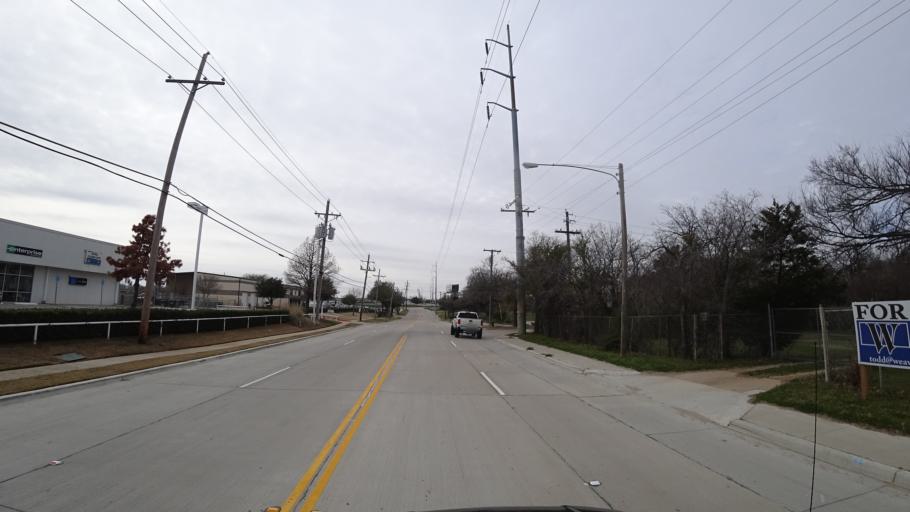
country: US
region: Texas
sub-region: Denton County
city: Lewisville
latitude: 33.0274
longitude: -96.9868
